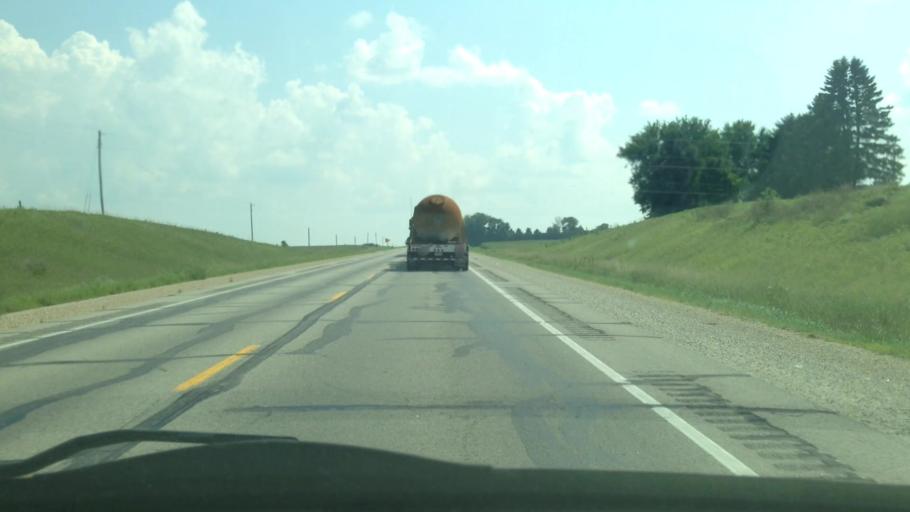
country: US
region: Iowa
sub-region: Chickasaw County
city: New Hampton
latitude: 43.1638
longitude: -92.2988
